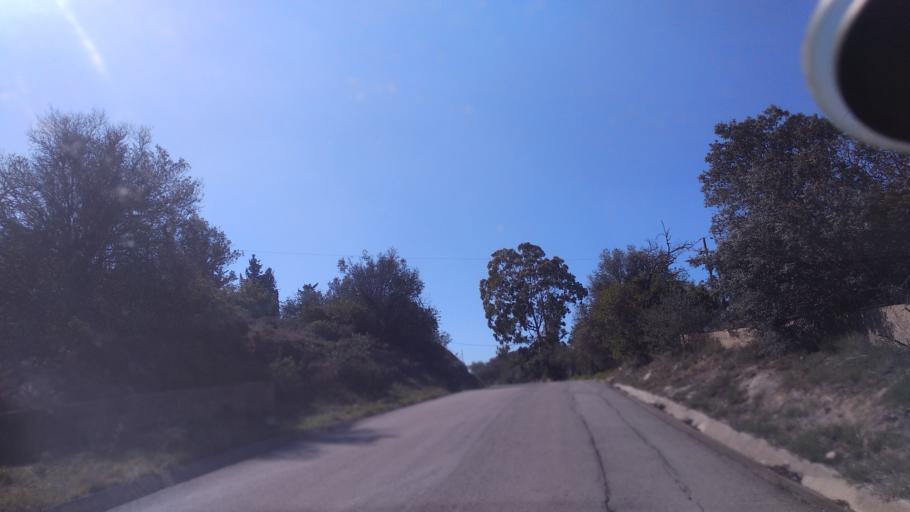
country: PT
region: Faro
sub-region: Faro
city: Santa Barbara de Nexe
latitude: 37.1144
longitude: -7.9316
